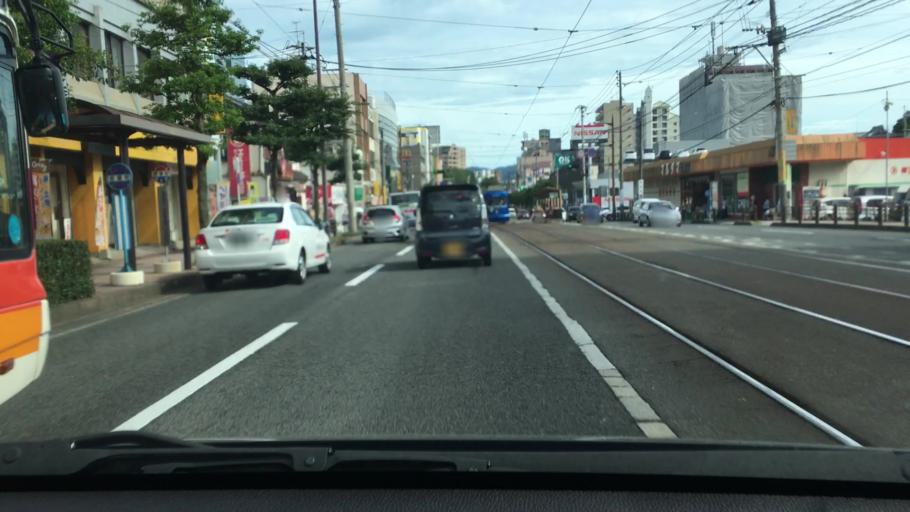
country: JP
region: Nagasaki
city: Obita
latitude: 32.7886
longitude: 129.8614
